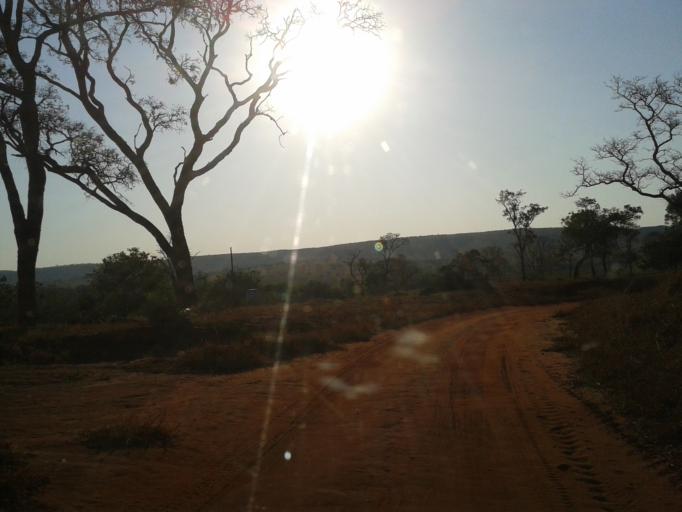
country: BR
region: Minas Gerais
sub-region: Ituiutaba
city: Ituiutaba
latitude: -19.2430
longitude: -49.6016
